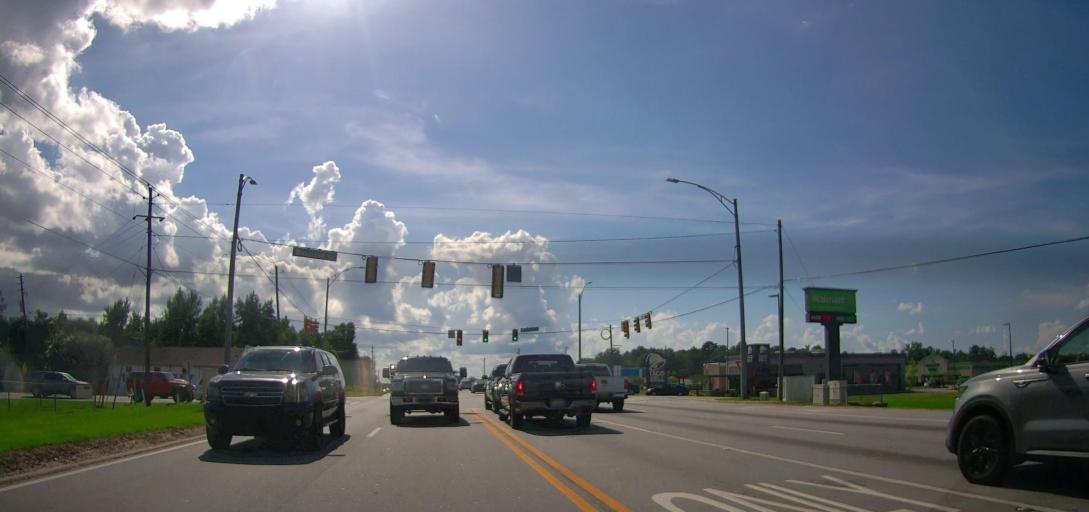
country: US
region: Alabama
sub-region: Russell County
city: Ladonia
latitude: 32.4694
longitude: -85.0842
